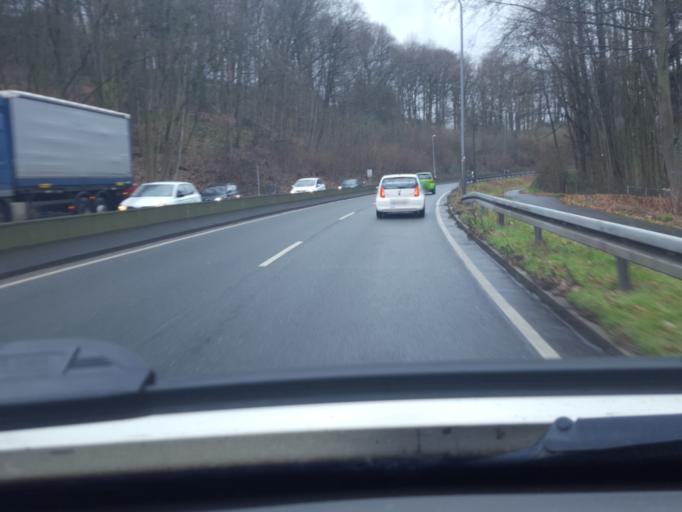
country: DE
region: North Rhine-Westphalia
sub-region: Regierungsbezirk Dusseldorf
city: Essen
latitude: 51.3991
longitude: 6.9914
